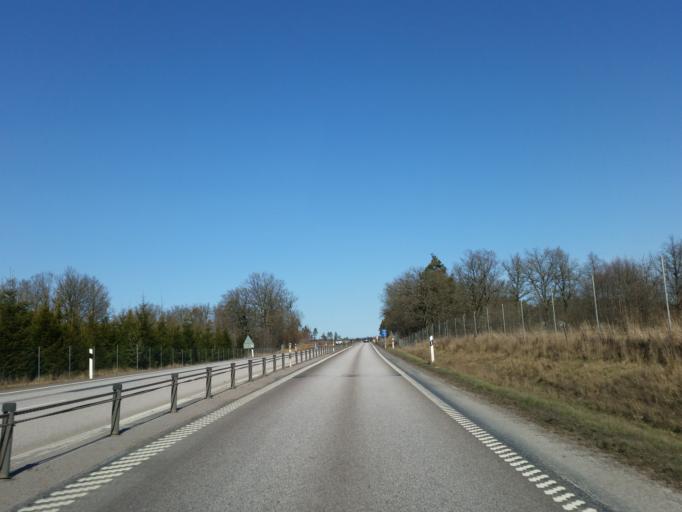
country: SE
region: Kalmar
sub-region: Monsteras Kommun
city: Moensteras
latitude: 57.0925
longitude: 16.4886
